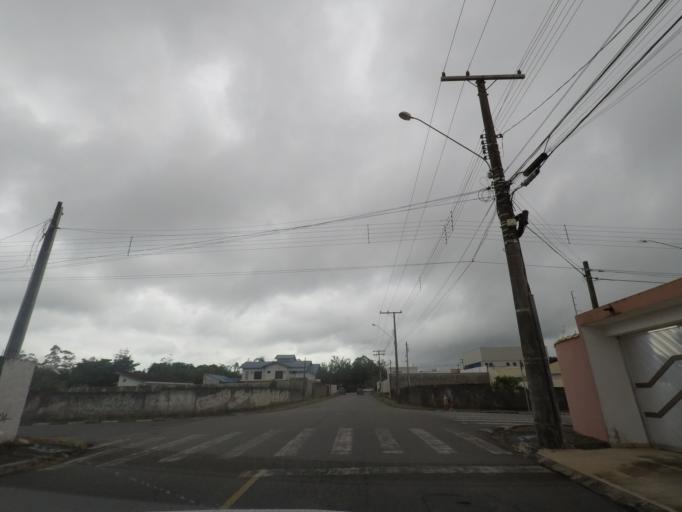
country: BR
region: Sao Paulo
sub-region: Registro
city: Registro
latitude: -24.5044
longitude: -47.8556
